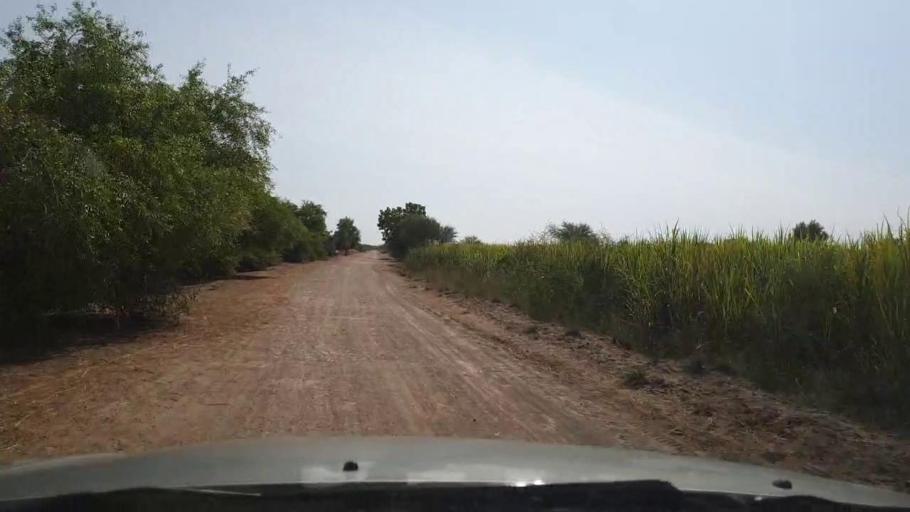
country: PK
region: Sindh
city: Bulri
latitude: 25.0078
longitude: 68.3203
